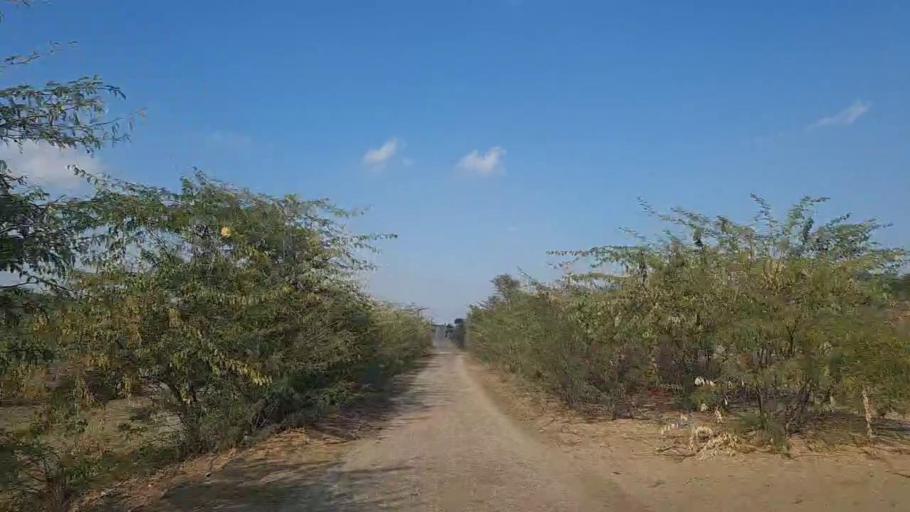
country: PK
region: Sindh
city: Tando Mittha Khan
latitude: 25.9971
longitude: 69.2443
